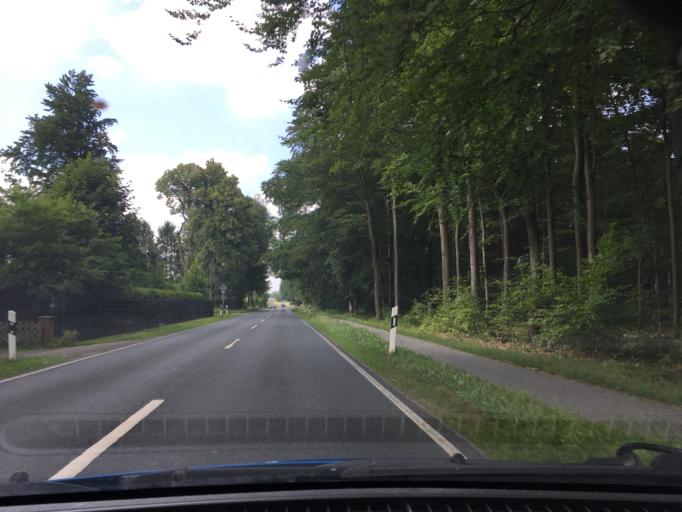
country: DE
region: Lower Saxony
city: Bendestorf
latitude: 53.3493
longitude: 9.9405
